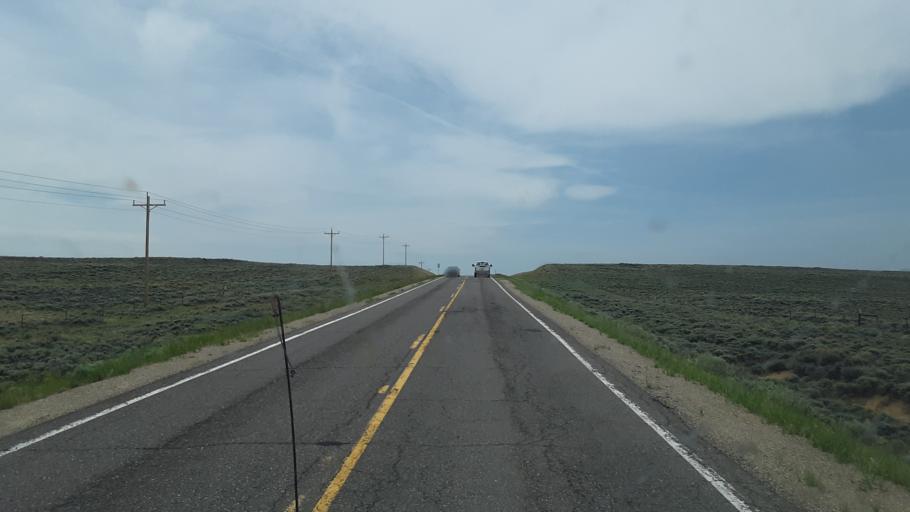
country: US
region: Colorado
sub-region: Jackson County
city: Walden
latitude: 40.6840
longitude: -106.3643
